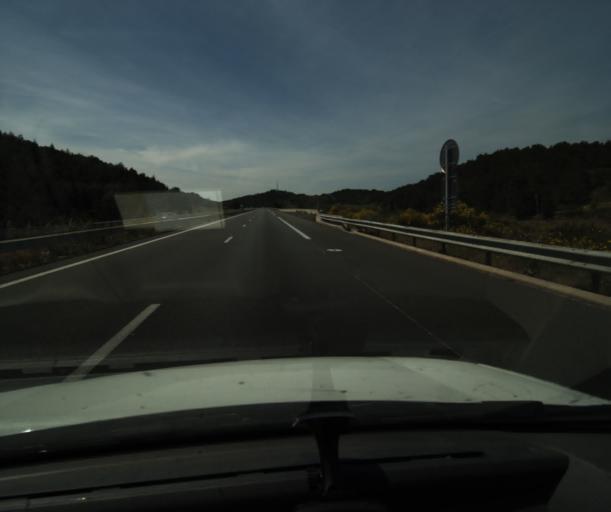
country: FR
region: Languedoc-Roussillon
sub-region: Departement de l'Aude
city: Puicheric
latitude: 43.1743
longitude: 2.6480
